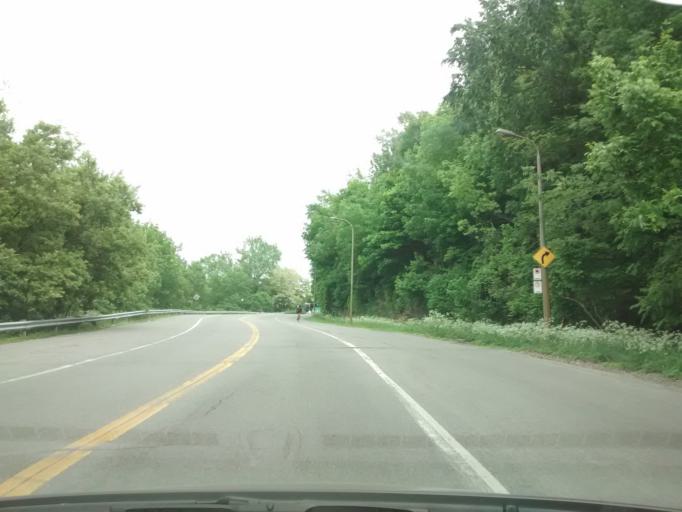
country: CA
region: Quebec
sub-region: Montreal
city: Montreal
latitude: 45.5113
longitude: -73.5956
